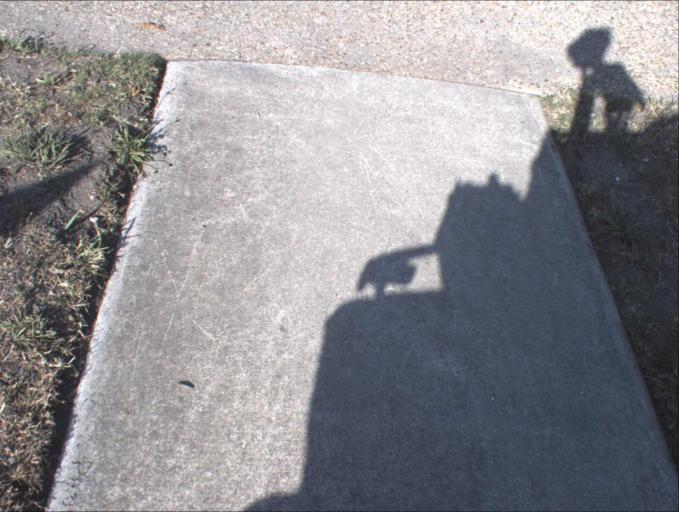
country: AU
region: Queensland
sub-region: Logan
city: Beenleigh
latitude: -27.6967
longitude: 153.1812
